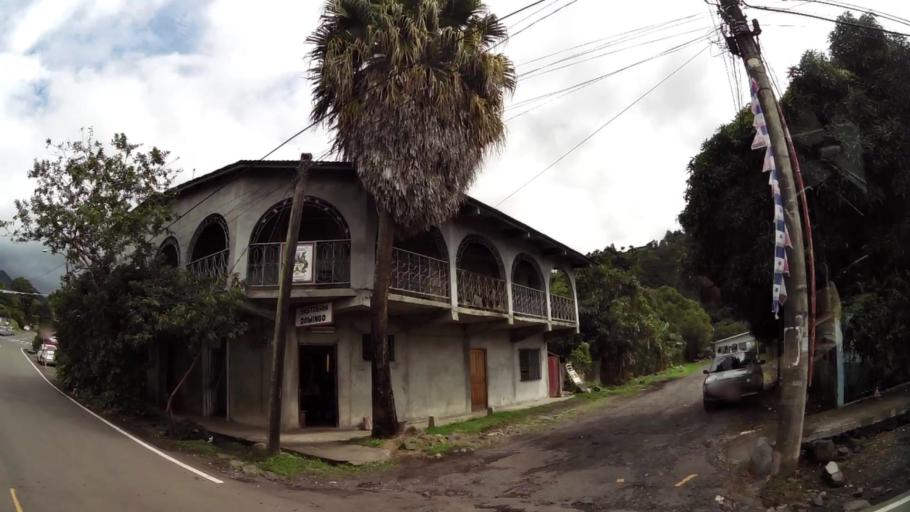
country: PA
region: Chiriqui
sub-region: Distrito Boquete
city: Boquete
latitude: 8.7788
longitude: -82.4321
